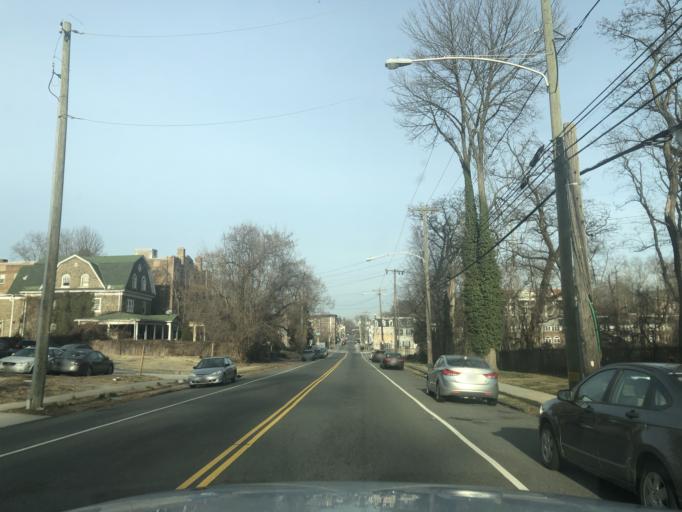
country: US
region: Pennsylvania
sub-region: Montgomery County
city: Bala-Cynwyd
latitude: 40.0215
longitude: -75.1793
